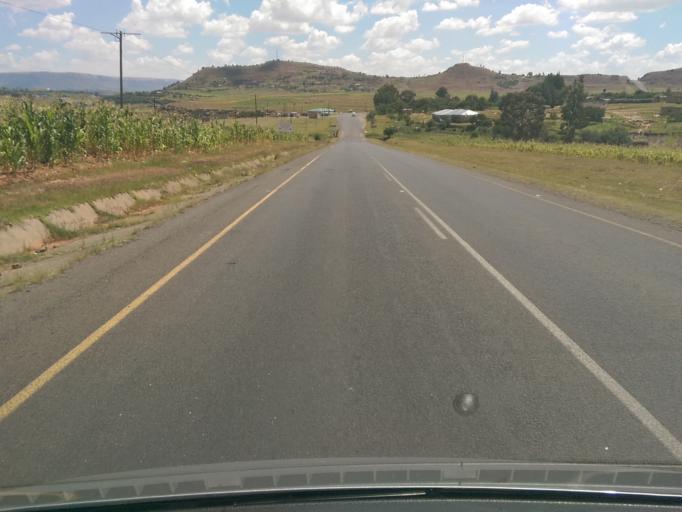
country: LS
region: Maseru
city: Maseru
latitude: -29.4201
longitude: 27.6496
